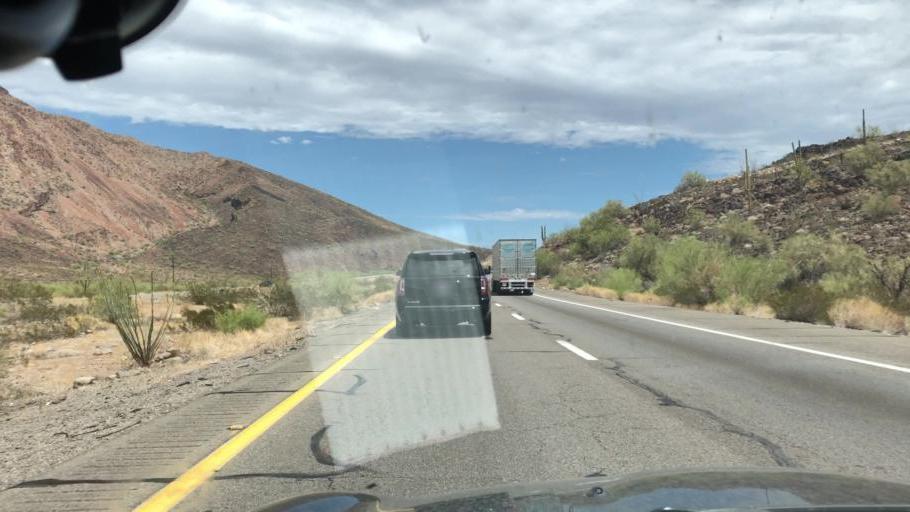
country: US
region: Arizona
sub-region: La Paz County
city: Quartzsite
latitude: 33.6771
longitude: -114.0588
